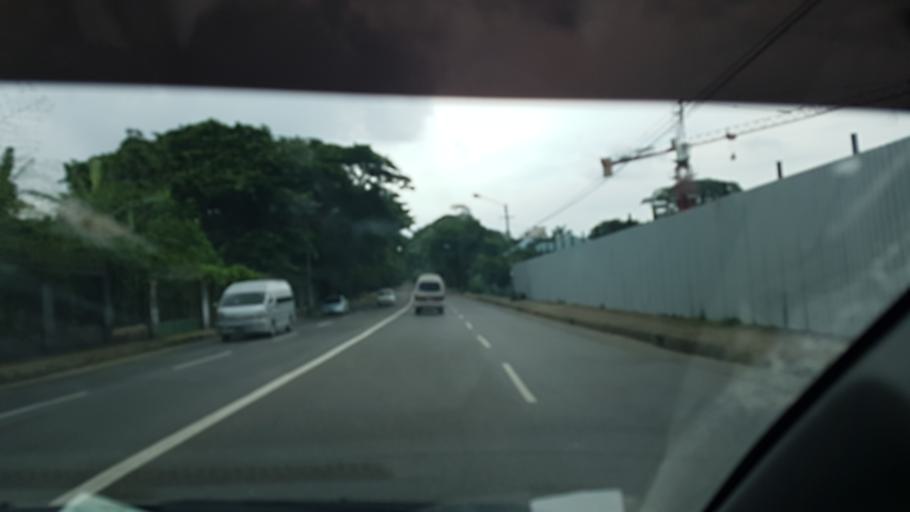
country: MM
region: Yangon
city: Yangon
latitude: 16.7918
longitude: 96.1364
